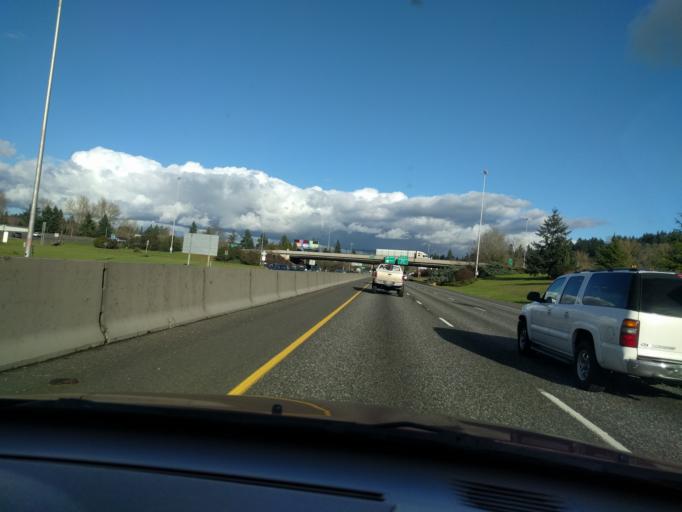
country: US
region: Oregon
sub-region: Clackamas County
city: Gladstone
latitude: 45.3735
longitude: -122.5892
